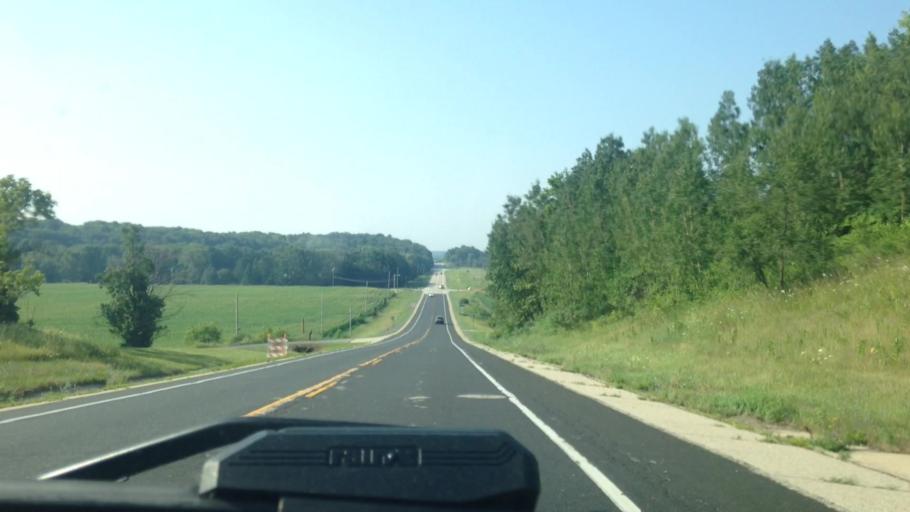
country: US
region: Wisconsin
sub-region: Waukesha County
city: Merton
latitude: 43.2122
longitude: -88.2617
